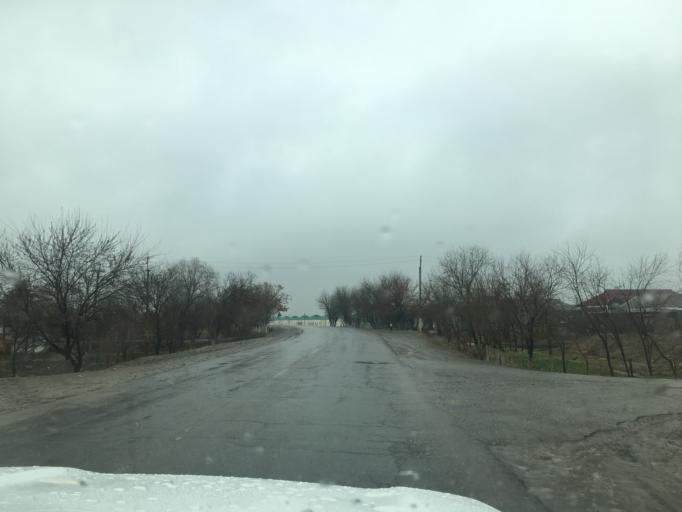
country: TM
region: Mary
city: Yoloeten
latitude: 37.2956
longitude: 62.3330
